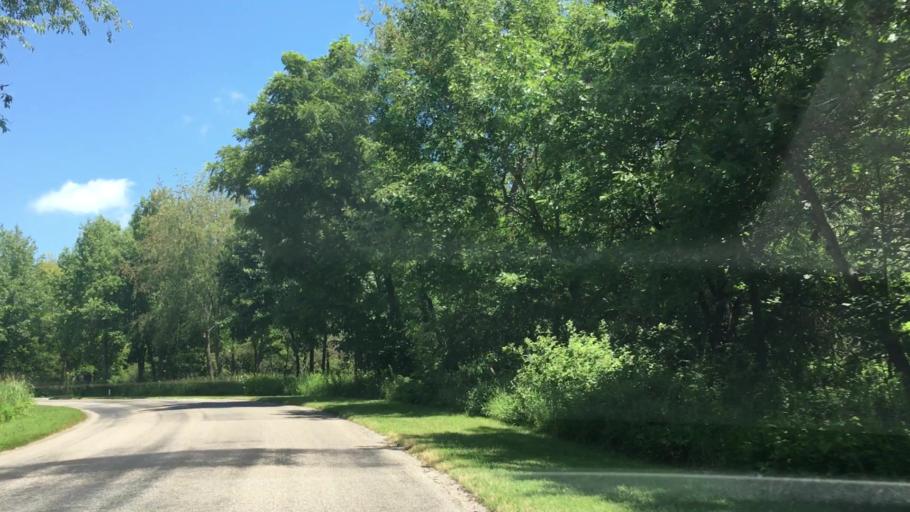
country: US
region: Iowa
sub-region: Johnson County
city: Tiffin
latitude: 41.7312
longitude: -91.7246
